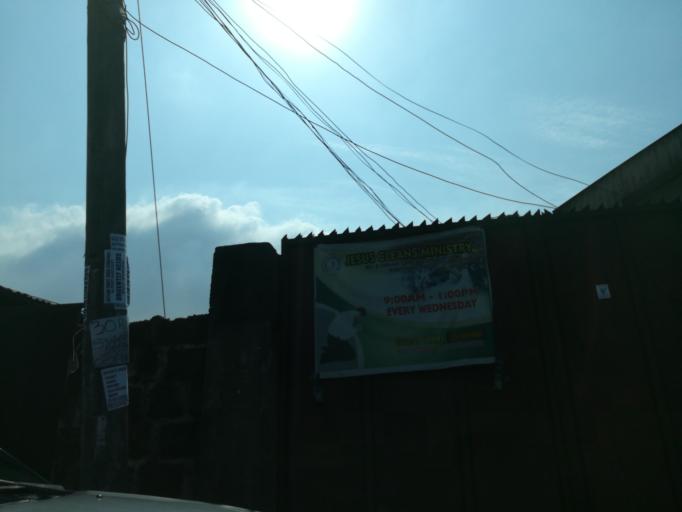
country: NG
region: Rivers
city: Port Harcourt
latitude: 4.8299
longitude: 6.9830
